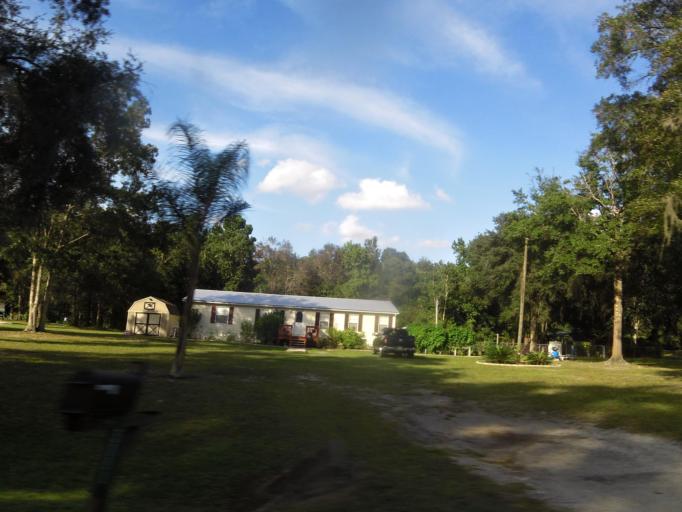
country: US
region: Florida
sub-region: Clay County
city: Green Cove Springs
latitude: 29.9106
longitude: -81.5165
